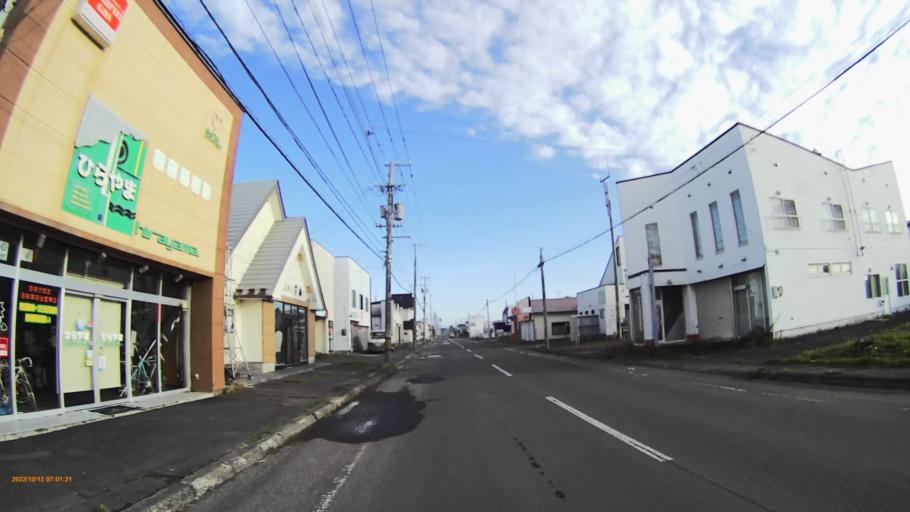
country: JP
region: Hokkaido
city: Kushiro
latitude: 42.8909
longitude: 143.9322
